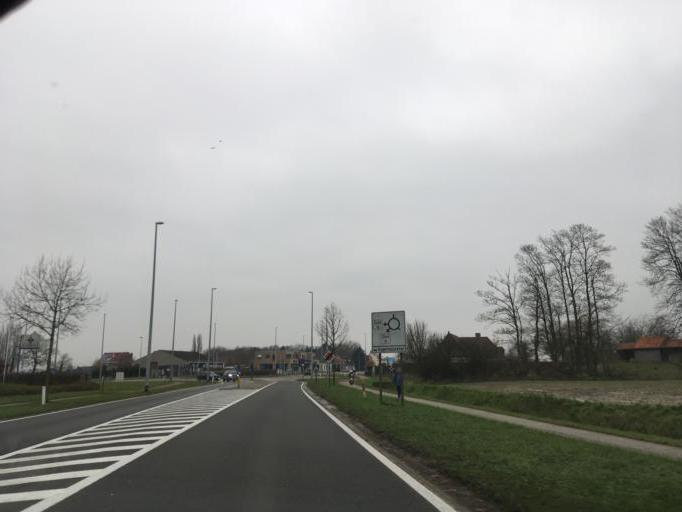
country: BE
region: Flanders
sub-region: Provincie West-Vlaanderen
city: Ingelmunster
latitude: 50.9323
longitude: 3.2528
